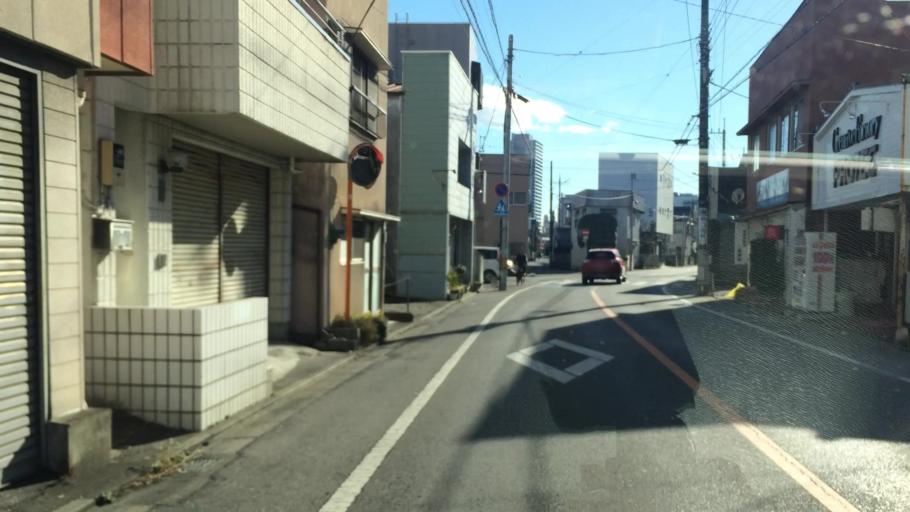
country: JP
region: Tochigi
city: Utsunomiya-shi
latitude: 36.5678
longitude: 139.8887
